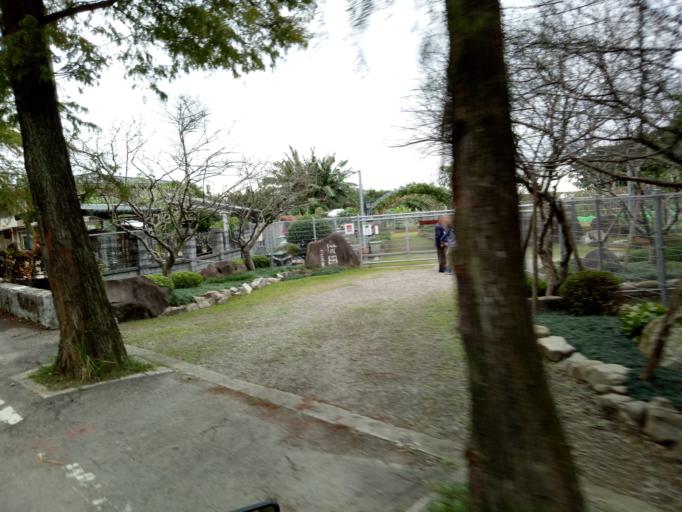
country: TW
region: Taiwan
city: Daxi
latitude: 24.8706
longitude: 121.2563
